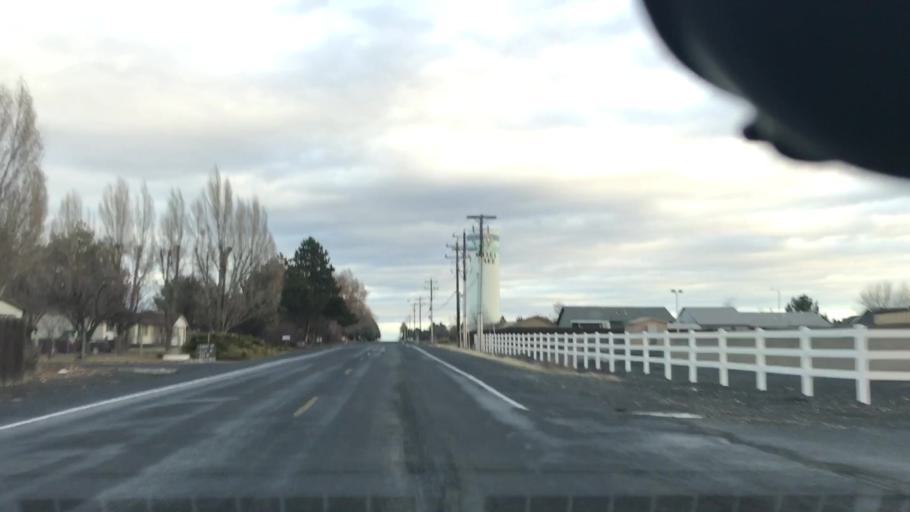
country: US
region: Washington
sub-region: Grant County
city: Moses Lake
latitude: 47.1164
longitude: -119.2519
